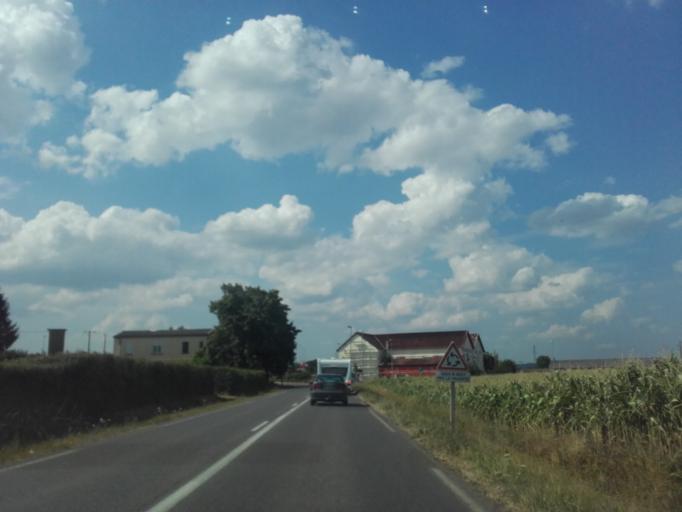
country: FR
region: Bourgogne
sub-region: Departement de Saone-et-Loire
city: Creches-sur-Saone
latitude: 46.2720
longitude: 4.7792
